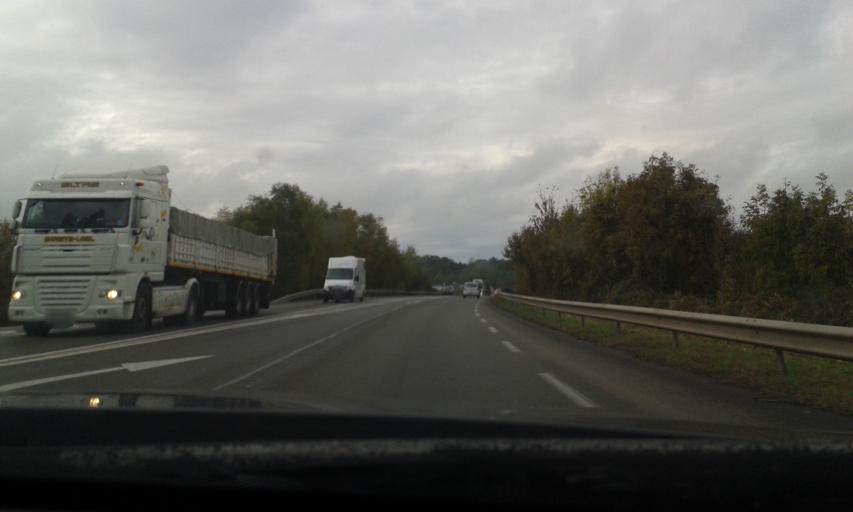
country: FR
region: Centre
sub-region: Departement d'Eure-et-Loir
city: Saint-Lubin-des-Joncherets
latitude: 48.7623
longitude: 1.2263
